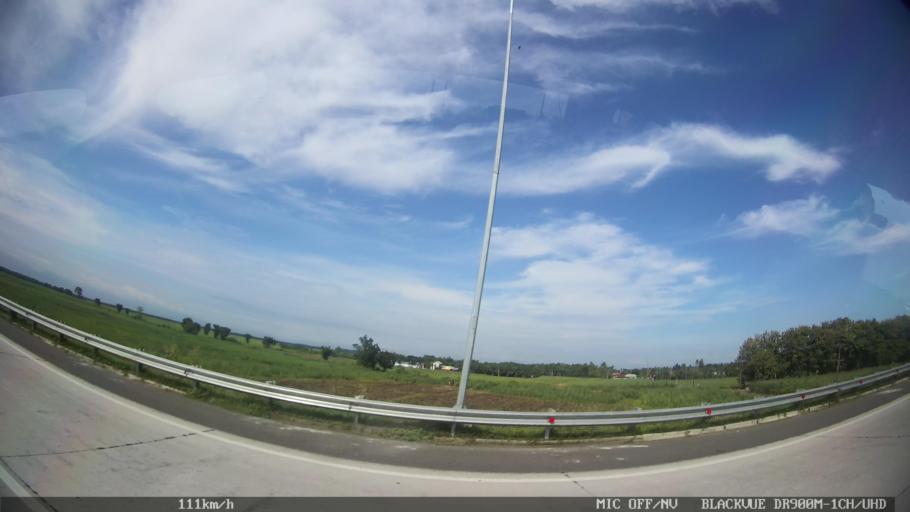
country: ID
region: North Sumatra
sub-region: Kabupaten Langkat
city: Stabat
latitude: 3.7010
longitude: 98.5397
